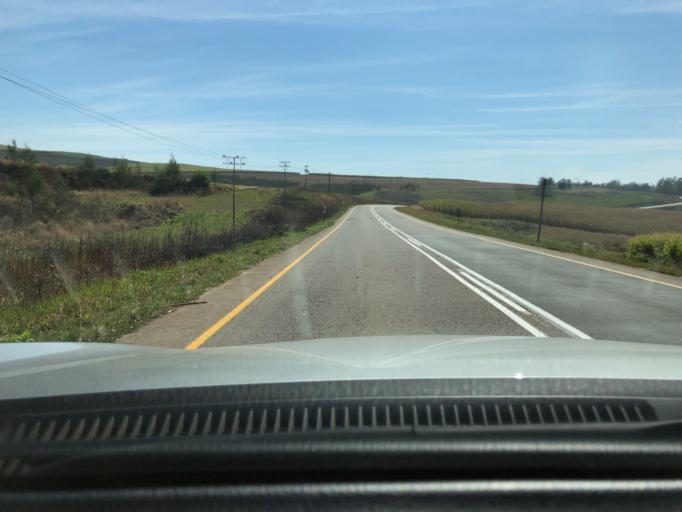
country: ZA
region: KwaZulu-Natal
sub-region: uMgungundlovu District Municipality
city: Richmond
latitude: -29.8049
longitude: 30.3431
